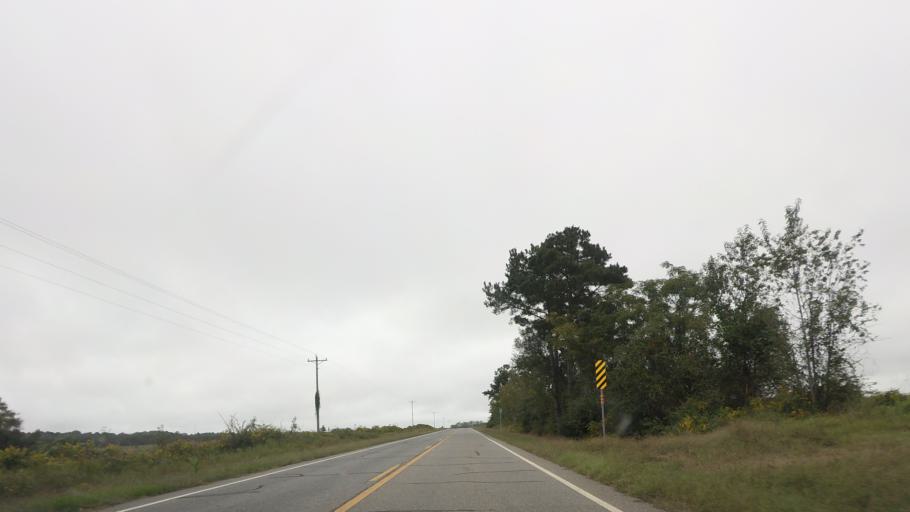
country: US
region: Georgia
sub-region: Irwin County
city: Ocilla
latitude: 31.5171
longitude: -83.2418
